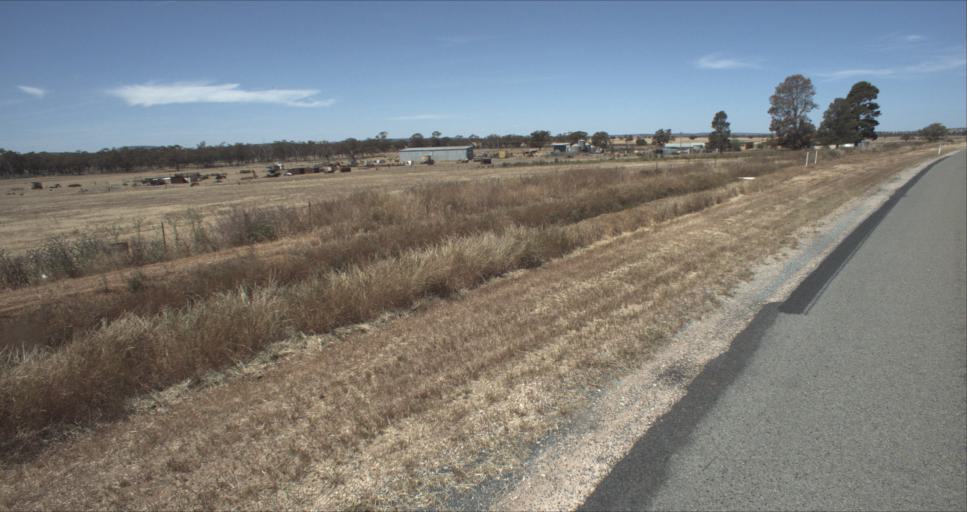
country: AU
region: New South Wales
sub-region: Leeton
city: Leeton
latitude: -34.5960
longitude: 146.4767
